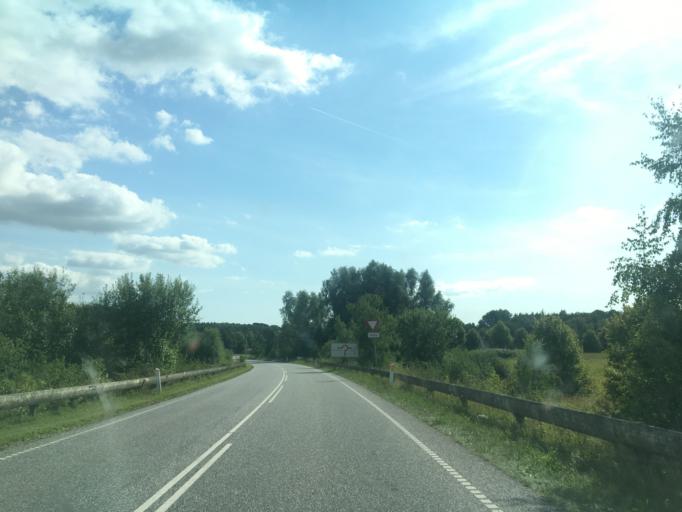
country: DK
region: South Denmark
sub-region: Middelfart Kommune
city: Ejby
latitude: 55.3948
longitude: 9.9635
